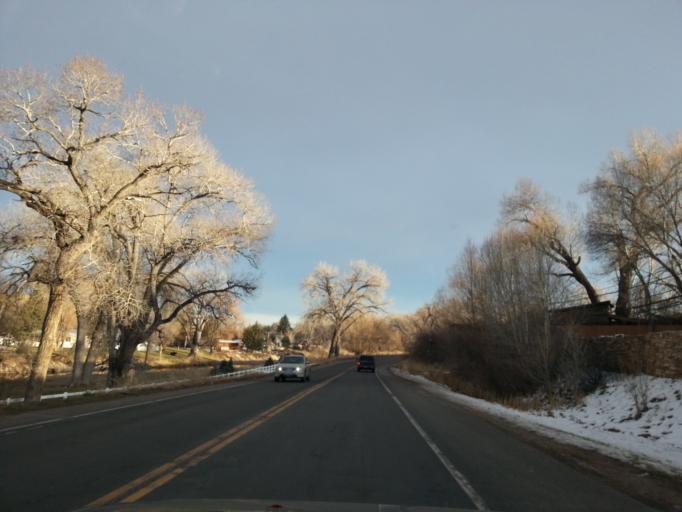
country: US
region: Colorado
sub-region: Larimer County
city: Loveland
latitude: 40.4155
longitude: -105.1718
